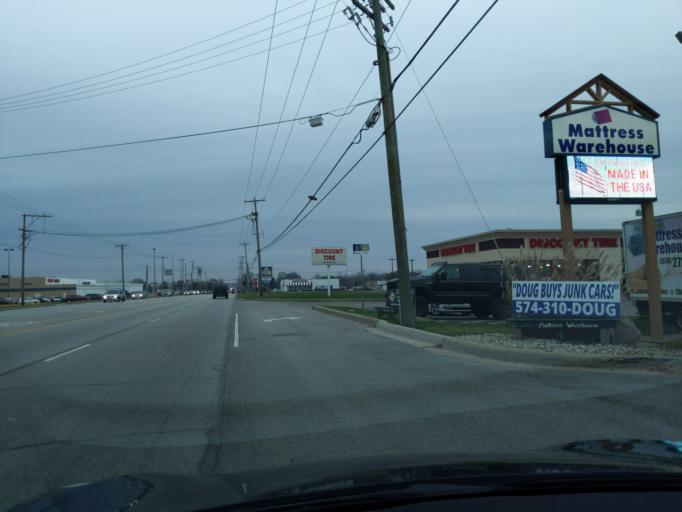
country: US
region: Indiana
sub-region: Saint Joseph County
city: Georgetown
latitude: 41.7121
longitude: -86.1877
